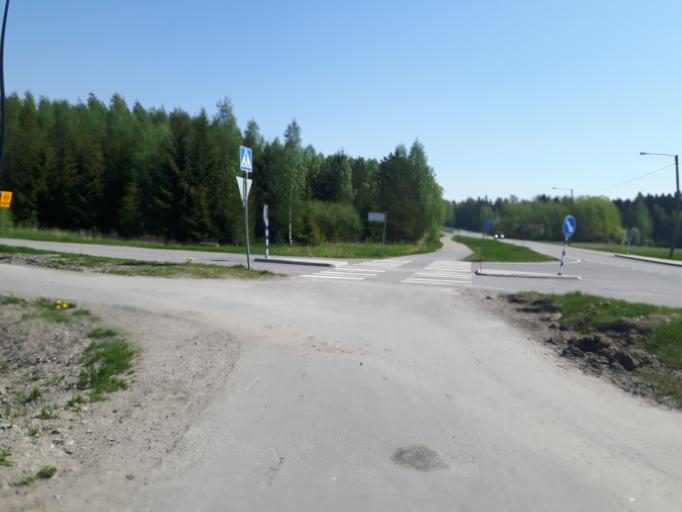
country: FI
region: Uusimaa
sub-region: Helsinki
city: Nickby
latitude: 60.2977
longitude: 25.3434
